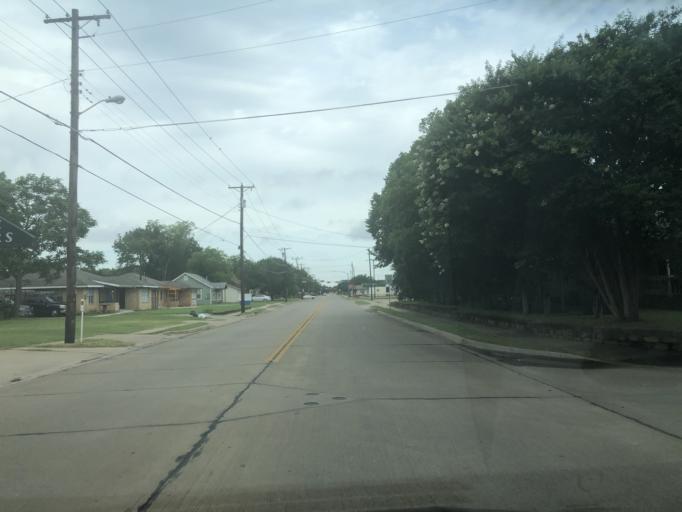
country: US
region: Texas
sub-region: Dallas County
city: Irving
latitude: 32.8086
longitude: -96.9448
